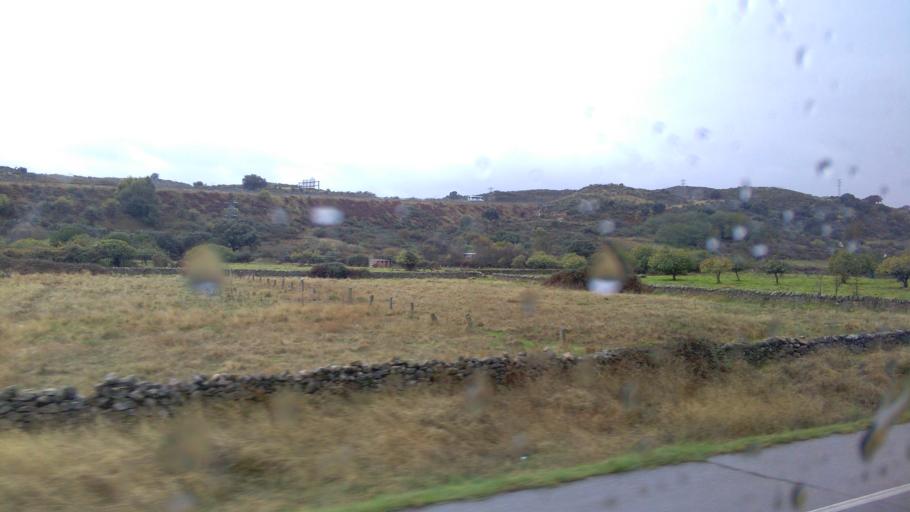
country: ES
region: Extremadura
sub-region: Provincia de Caceres
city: Navalmoral de la Mata
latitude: 39.8914
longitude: -5.5174
